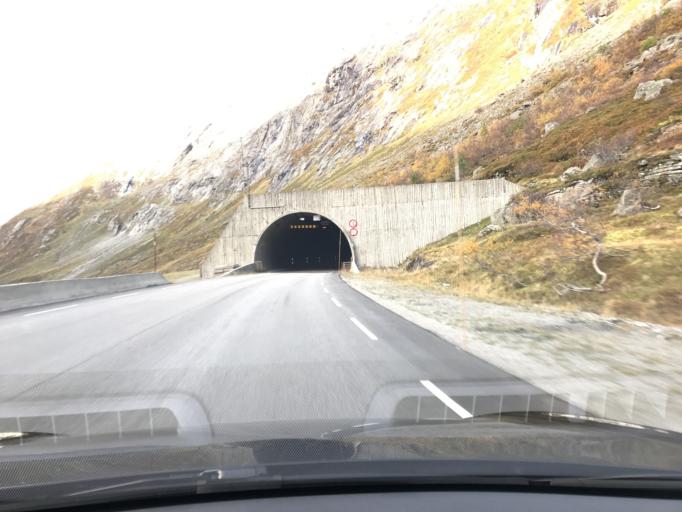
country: NO
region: More og Romsdal
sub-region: Norddal
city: Valldal
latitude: 61.9861
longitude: 7.3053
